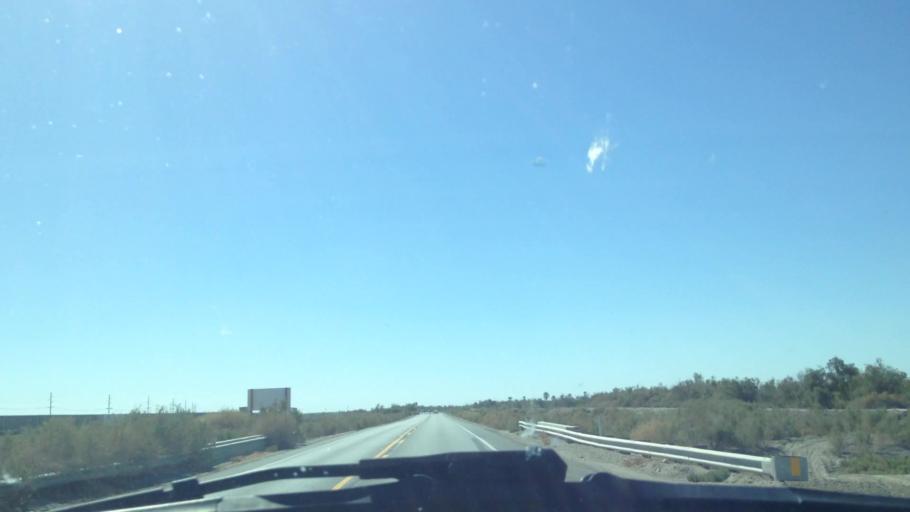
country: US
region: California
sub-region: Riverside County
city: Mecca
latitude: 33.5629
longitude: -116.0724
